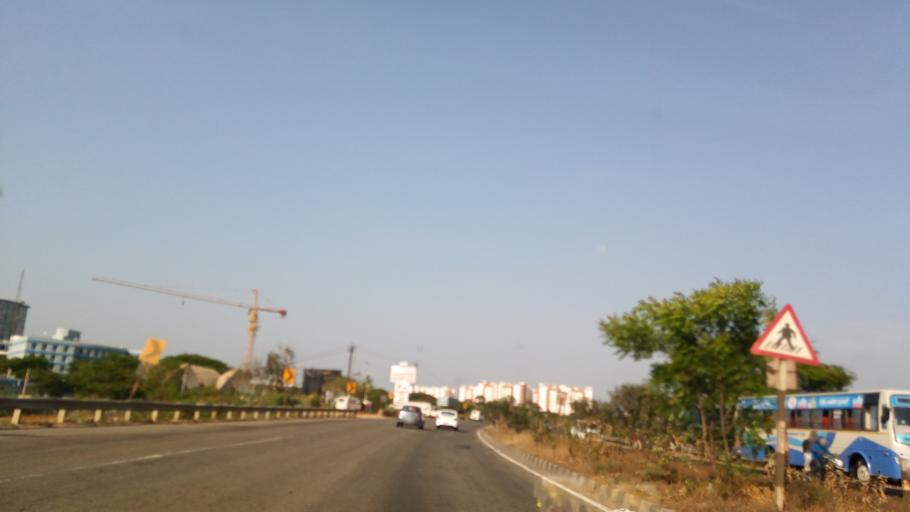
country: IN
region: Tamil Nadu
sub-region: Kancheepuram
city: Nandambakkam
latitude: 13.0217
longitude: 80.0158
